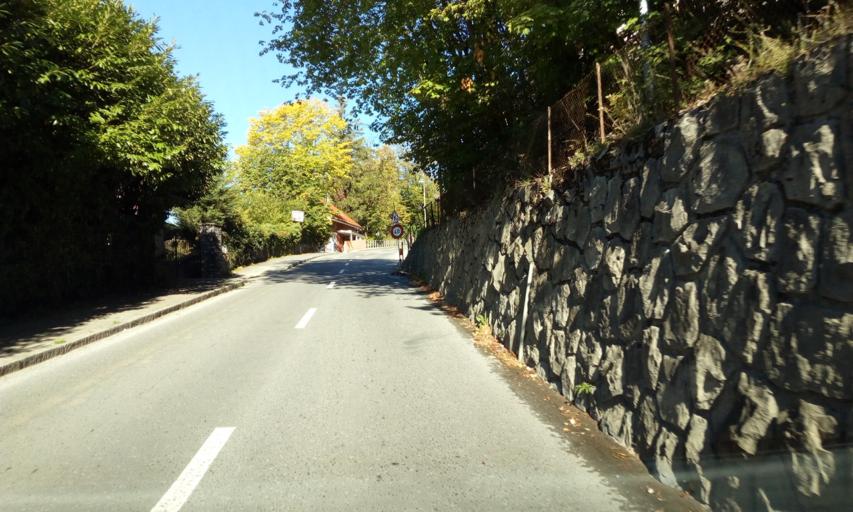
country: CH
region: Vaud
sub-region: Riviera-Pays-d'Enhaut District
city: Caux
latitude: 46.4292
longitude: 6.9256
